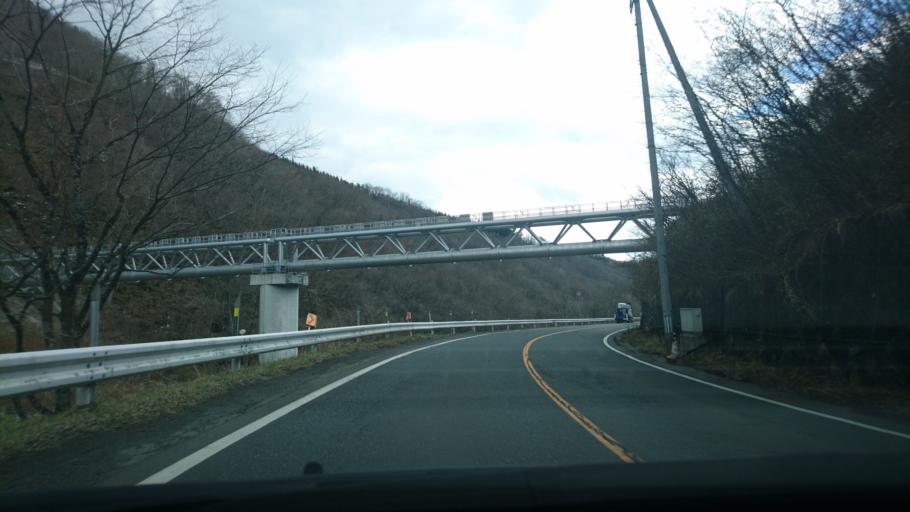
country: JP
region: Iwate
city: Hanamaki
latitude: 39.3612
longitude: 141.2953
